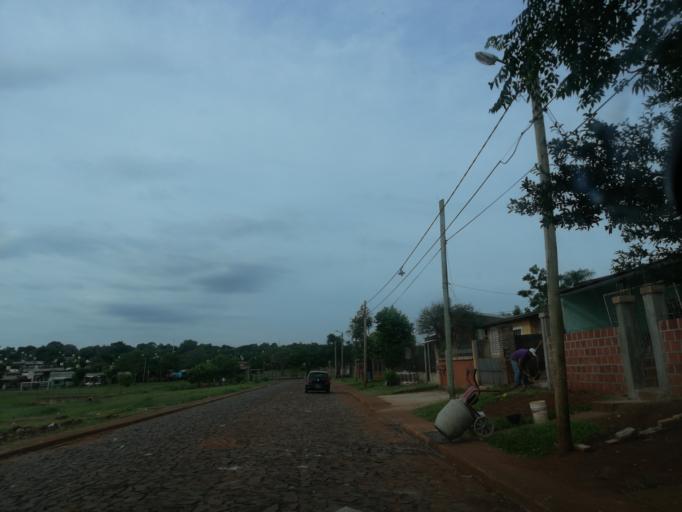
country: AR
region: Misiones
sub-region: Departamento de Capital
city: Posadas
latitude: -27.4304
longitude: -55.9093
